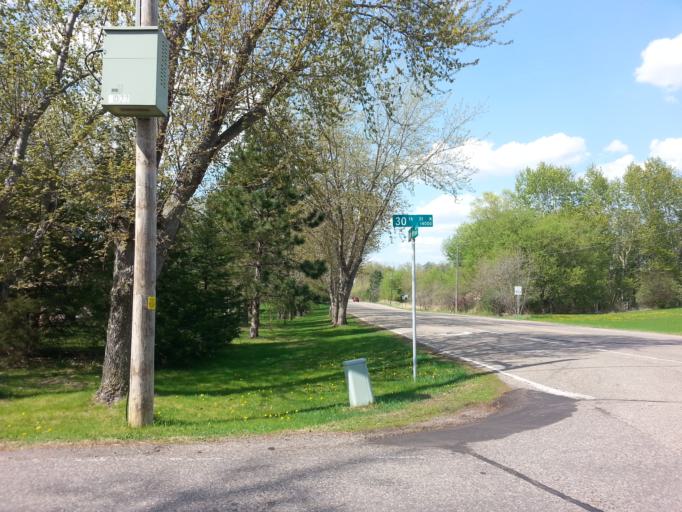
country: US
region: Minnesota
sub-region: Washington County
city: Oak Park Heights
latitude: 44.9926
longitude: -92.8226
